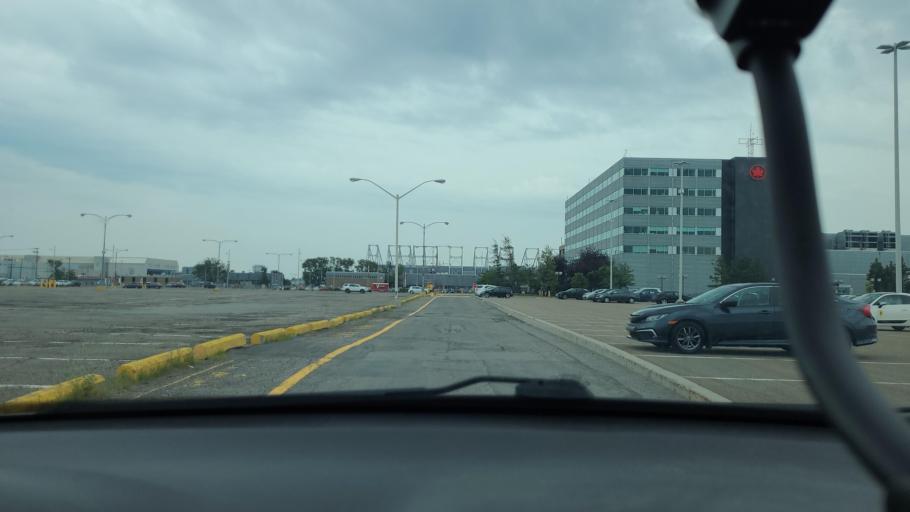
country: CA
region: Quebec
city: Dorval
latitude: 45.4737
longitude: -73.7380
